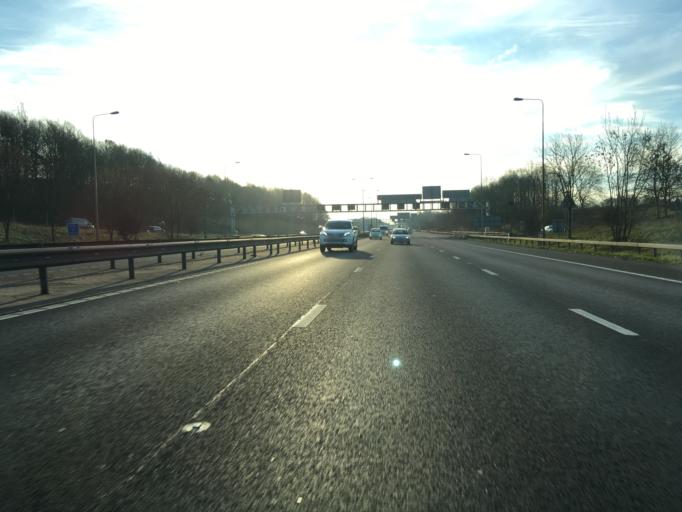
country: GB
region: England
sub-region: Staffordshire
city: Essington
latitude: 52.6563
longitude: -2.0632
